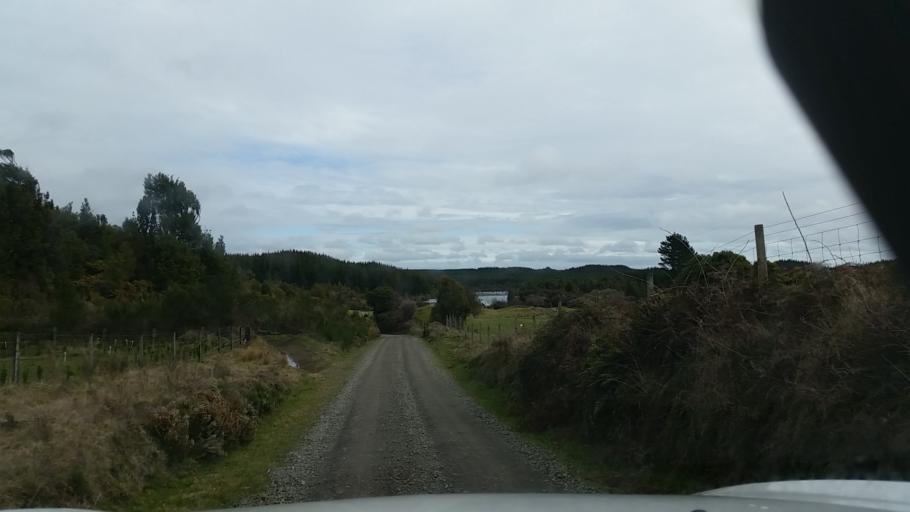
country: NZ
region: Bay of Plenty
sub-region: Rotorua District
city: Rotorua
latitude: -37.9881
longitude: 176.1641
